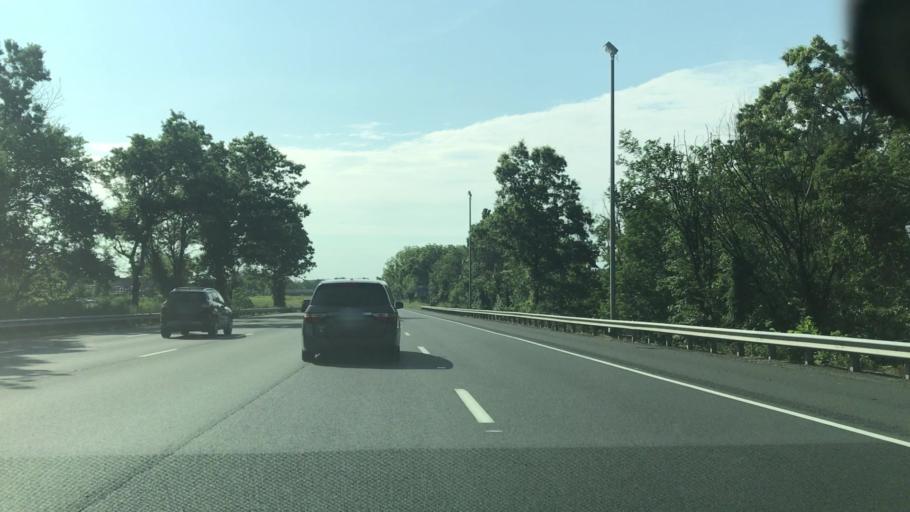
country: US
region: New Jersey
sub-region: Somerset County
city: Finderne
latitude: 40.5739
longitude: -74.5674
